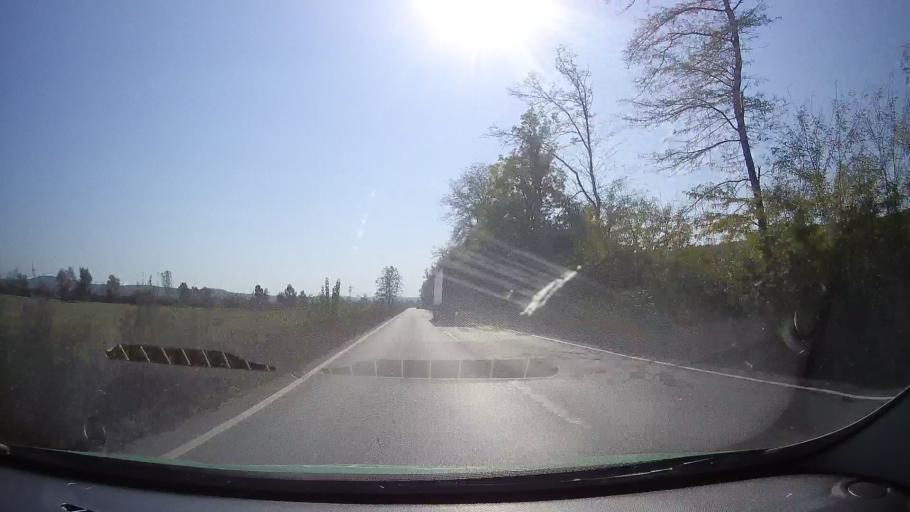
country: RO
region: Arad
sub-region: Comuna Ususau
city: Ususau
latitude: 46.1042
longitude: 21.8148
